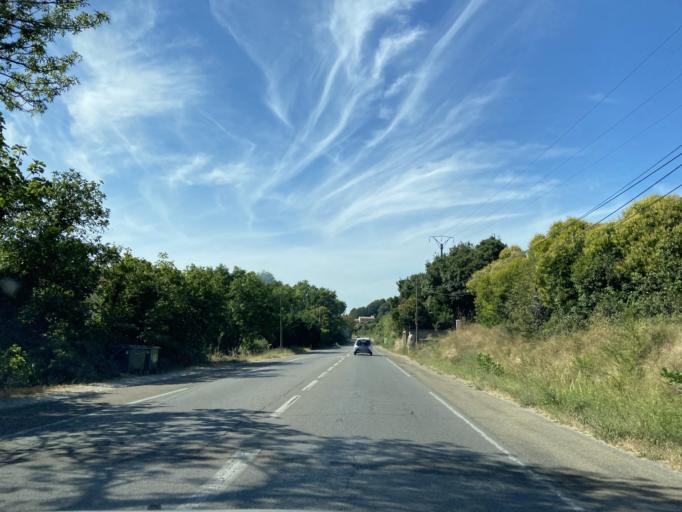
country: FR
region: Provence-Alpes-Cote d'Azur
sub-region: Departement des Bouches-du-Rhone
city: Saint-Chamas
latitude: 43.5593
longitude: 5.0313
